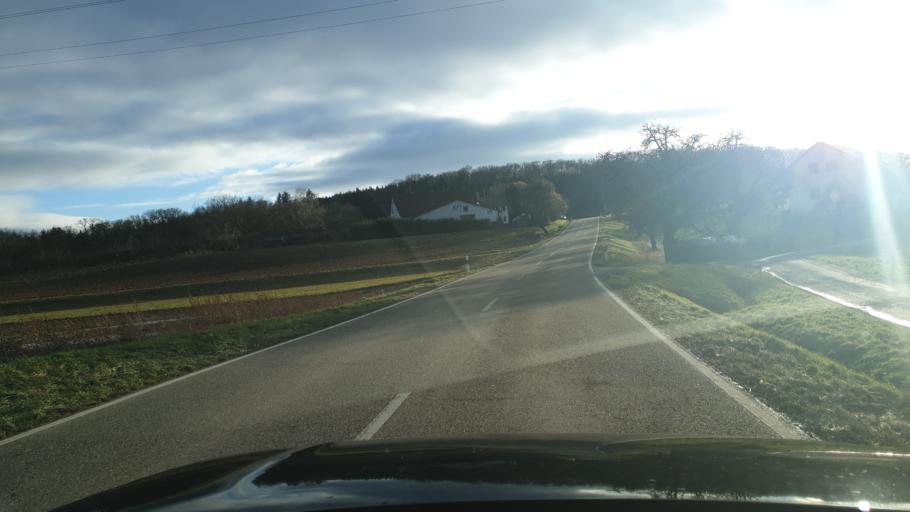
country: DE
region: Baden-Wuerttemberg
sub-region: Regierungsbezirk Stuttgart
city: Mundelsheim
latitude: 49.0102
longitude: 9.2497
